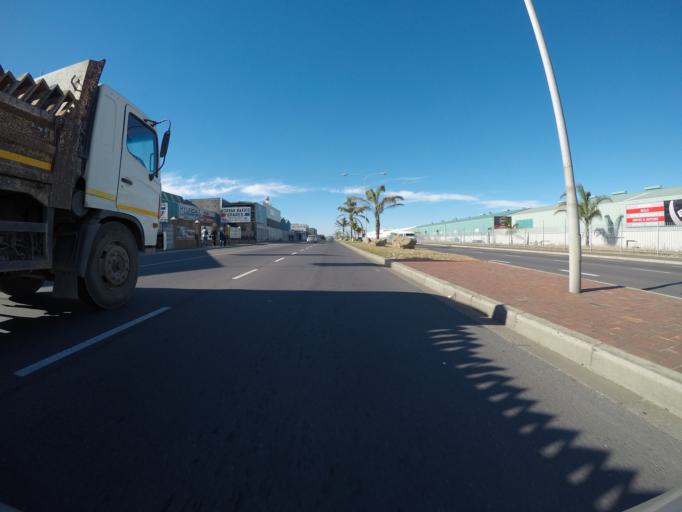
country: ZA
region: Western Cape
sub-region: City of Cape Town
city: Kraaifontein
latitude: -33.9025
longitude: 18.6690
